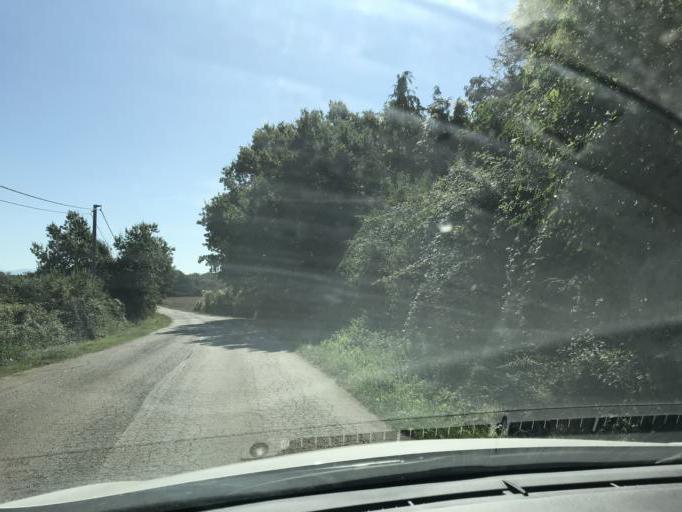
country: IT
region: Umbria
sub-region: Provincia di Terni
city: Avigliano Umbro
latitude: 42.6180
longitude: 12.4213
